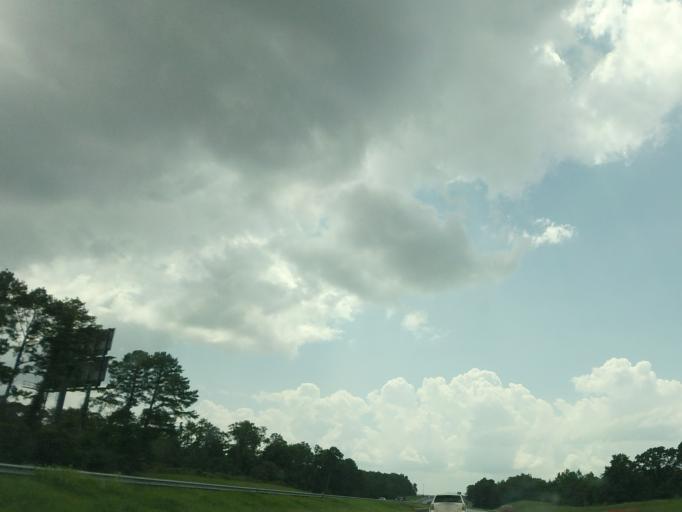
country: US
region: Georgia
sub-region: Houston County
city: Centerville
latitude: 32.5582
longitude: -83.7443
